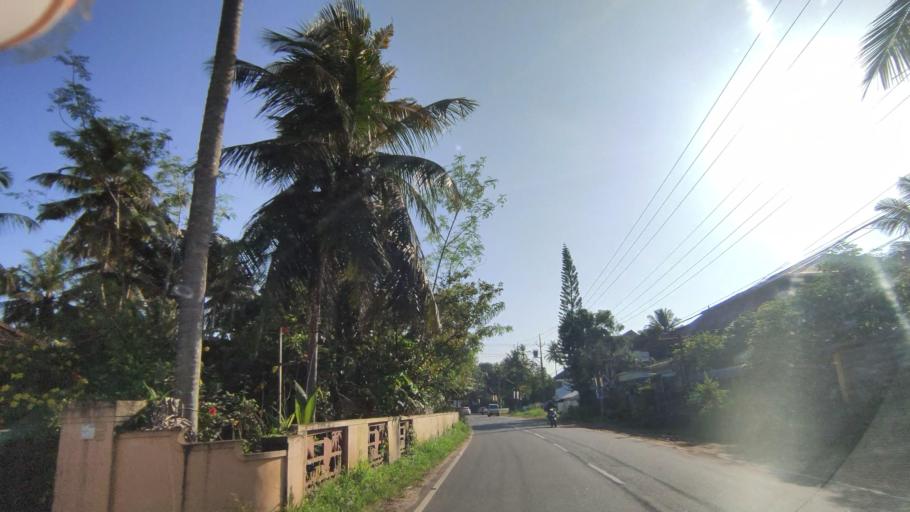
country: IN
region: Kerala
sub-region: Kottayam
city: Kottayam
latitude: 9.5914
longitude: 76.4937
